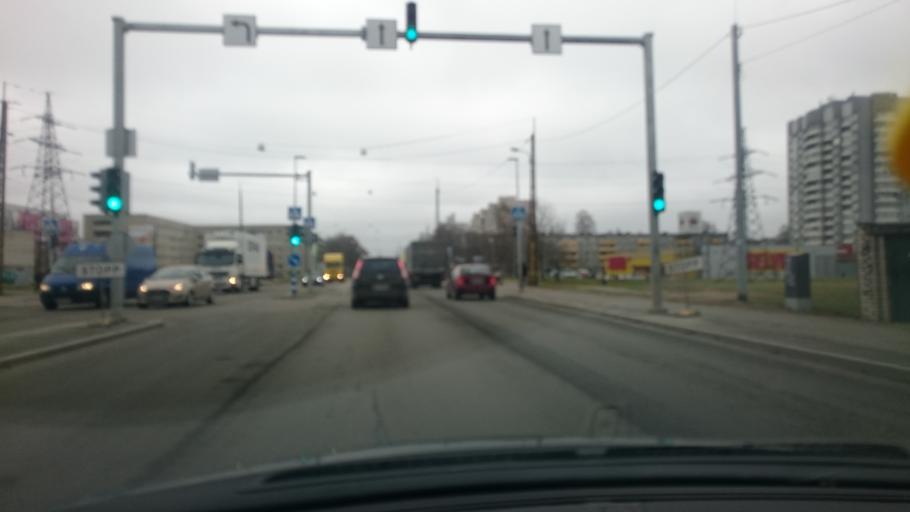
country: EE
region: Harju
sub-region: Tallinna linn
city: Tallinn
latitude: 59.4465
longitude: 24.7006
